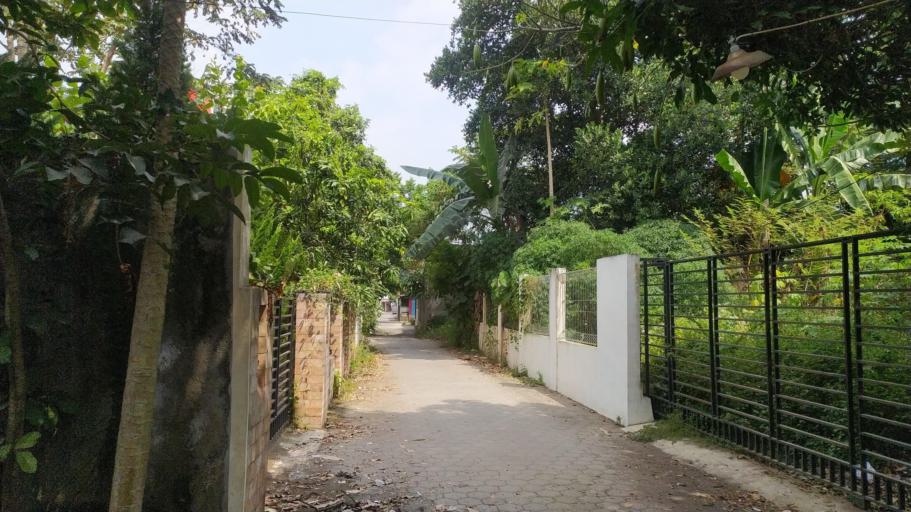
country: ID
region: Daerah Istimewa Yogyakarta
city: Depok
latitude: -7.7675
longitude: 110.4256
